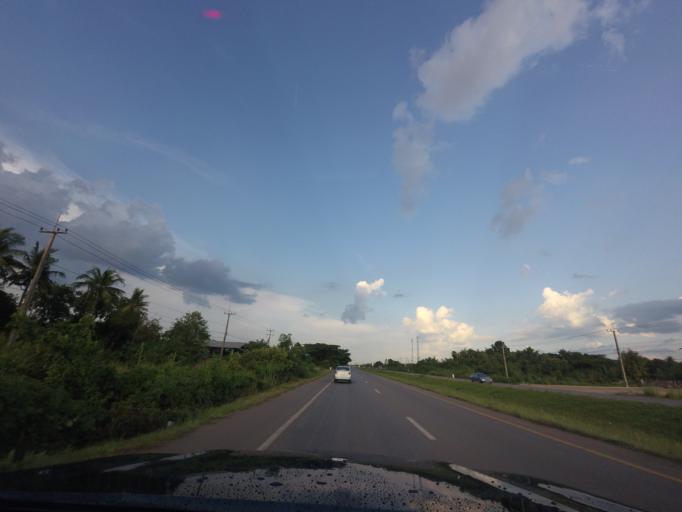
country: TH
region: Khon Kaen
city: Khon Kaen
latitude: 16.3942
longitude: 102.8523
